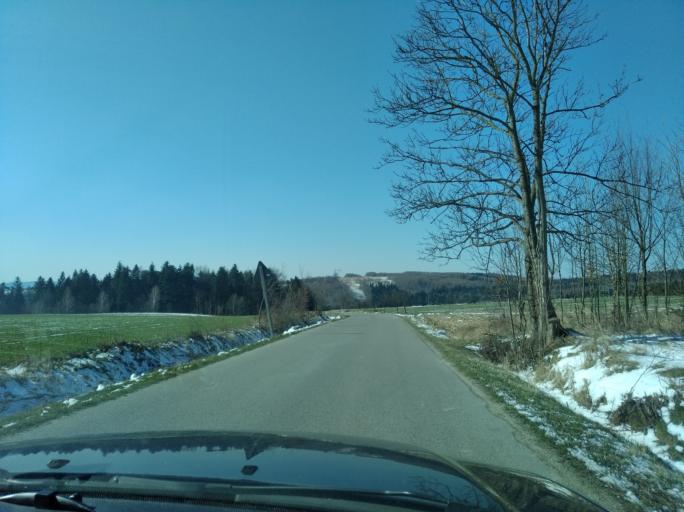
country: PL
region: Subcarpathian Voivodeship
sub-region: Powiat strzyzowski
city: Jawornik
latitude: 49.8635
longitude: 21.8708
